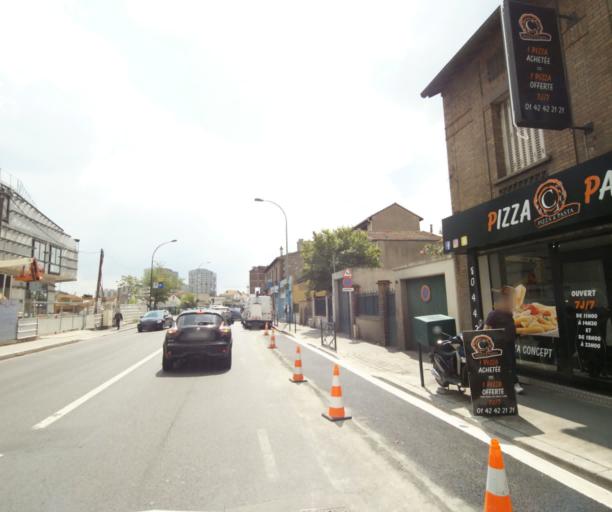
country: FR
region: Ile-de-France
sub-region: Departement des Hauts-de-Seine
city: Bois-Colombes
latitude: 48.9322
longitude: 2.2661
